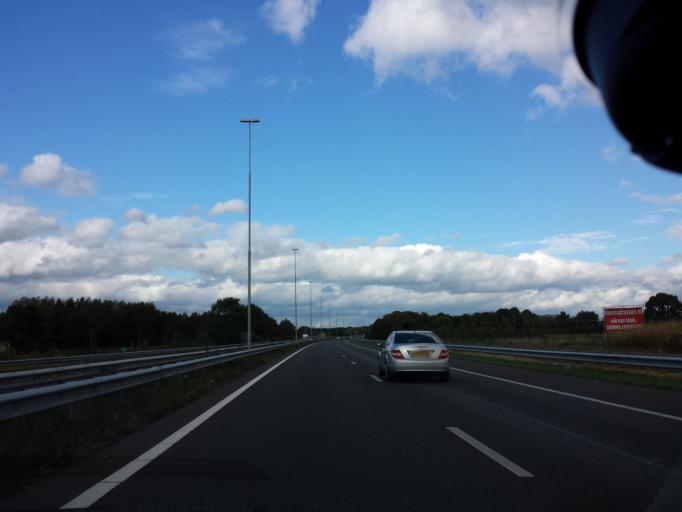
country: NL
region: North Brabant
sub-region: Gemeente Cuijk
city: Cuijk
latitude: 51.7031
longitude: 5.8780
